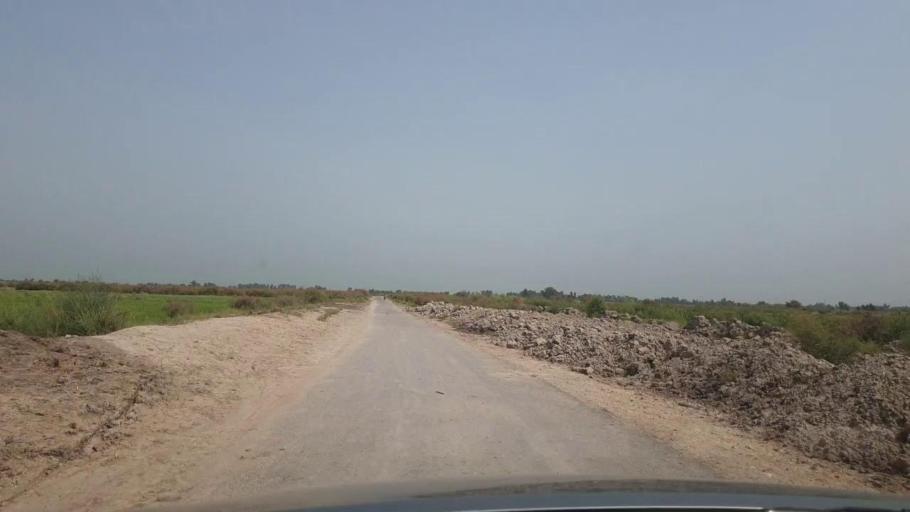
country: PK
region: Sindh
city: Madeji
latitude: 27.8289
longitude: 68.4470
